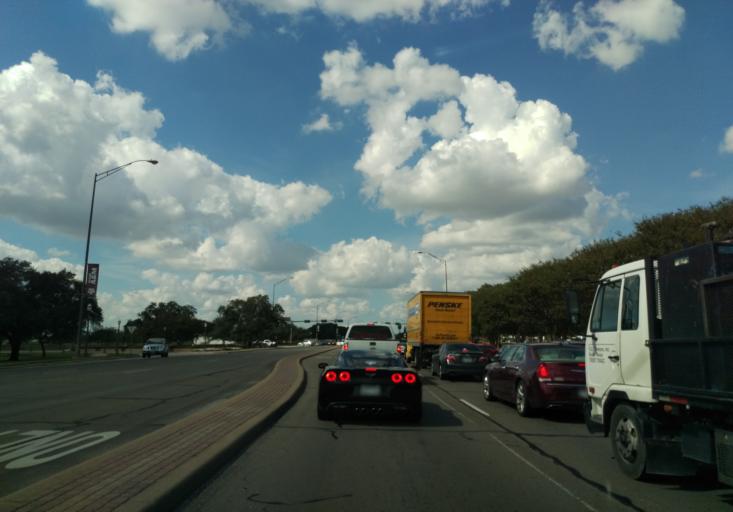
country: US
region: Texas
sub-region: Brazos County
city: College Station
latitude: 30.6225
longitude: -96.3285
